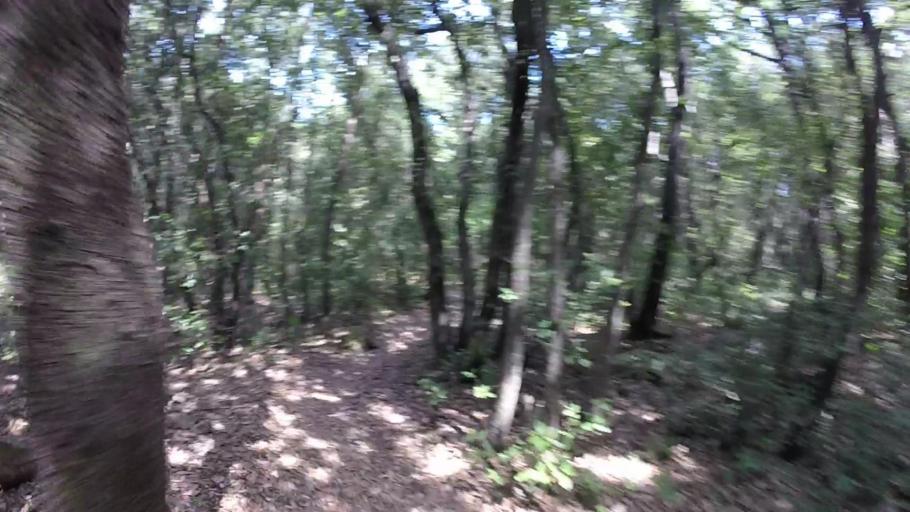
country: FR
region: Provence-Alpes-Cote d'Azur
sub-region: Departement des Alpes-Maritimes
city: Valbonne
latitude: 43.6262
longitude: 7.0275
